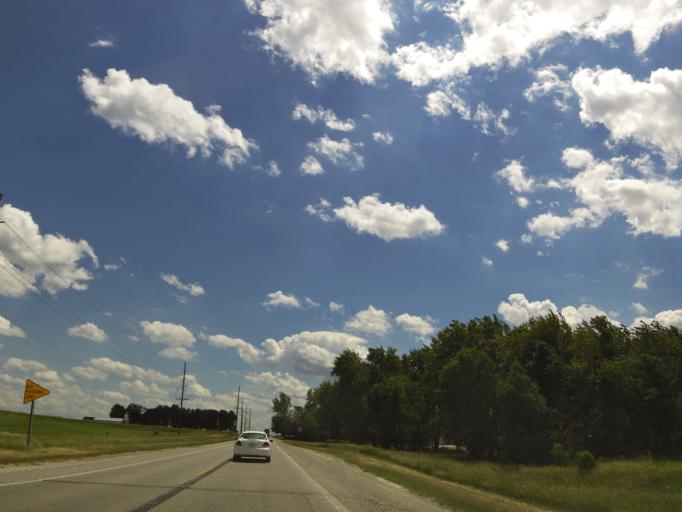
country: US
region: Iowa
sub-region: Buchanan County
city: Independence
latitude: 42.4236
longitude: -91.8898
